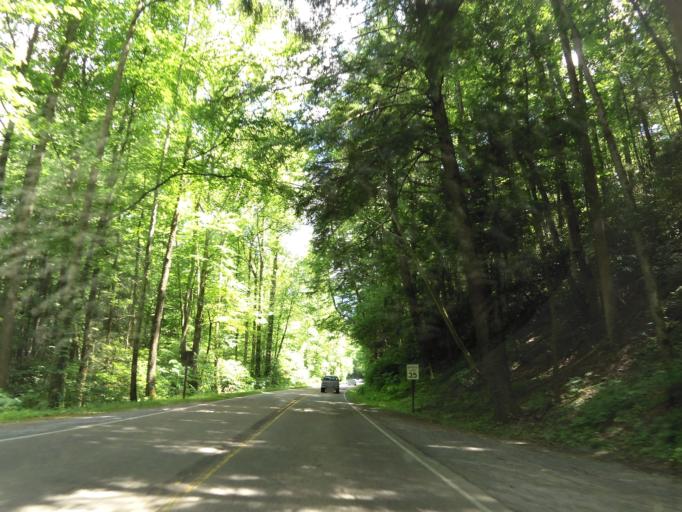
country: US
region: Tennessee
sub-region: Sevier County
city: Gatlinburg
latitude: 35.6817
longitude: -83.5331
